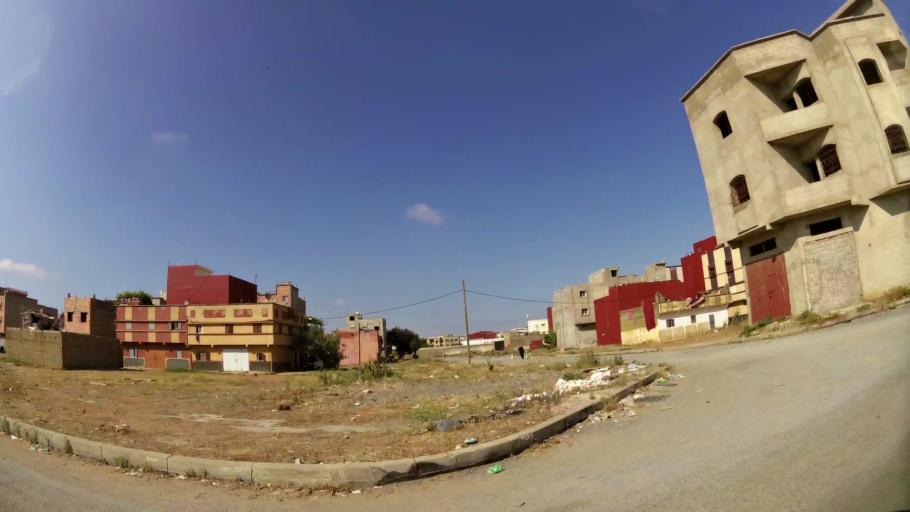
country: MA
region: Rabat-Sale-Zemmour-Zaer
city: Sale
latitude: 34.0627
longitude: -6.7674
